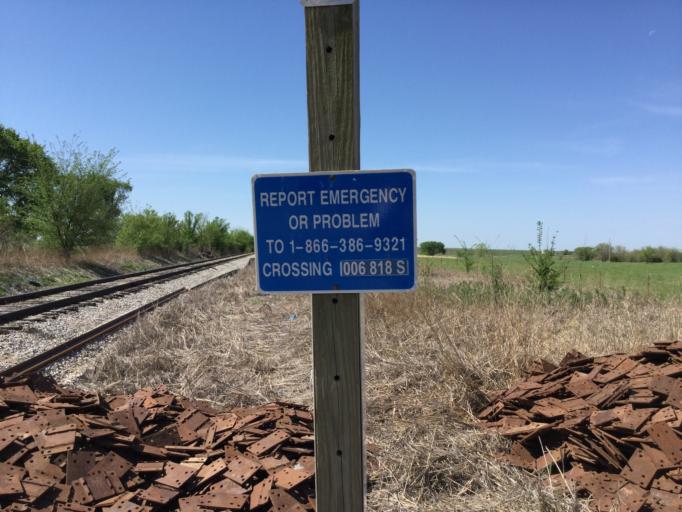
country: US
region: Kansas
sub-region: Montgomery County
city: Cherryvale
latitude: 37.3544
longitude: -95.5212
